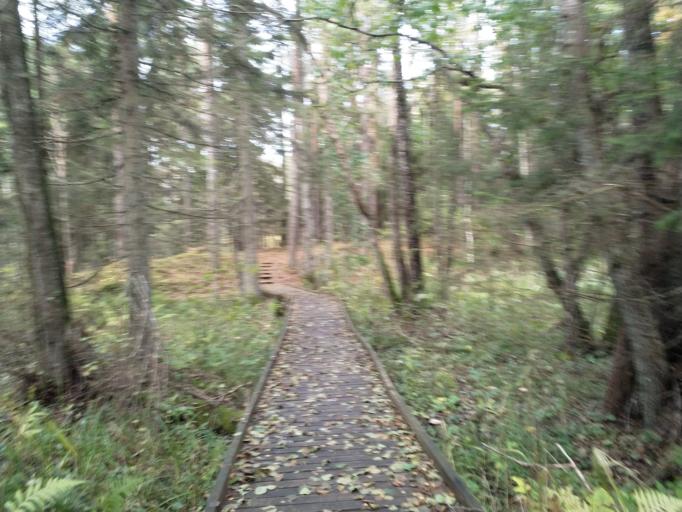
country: LV
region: Dundaga
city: Dundaga
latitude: 57.6474
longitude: 22.2595
